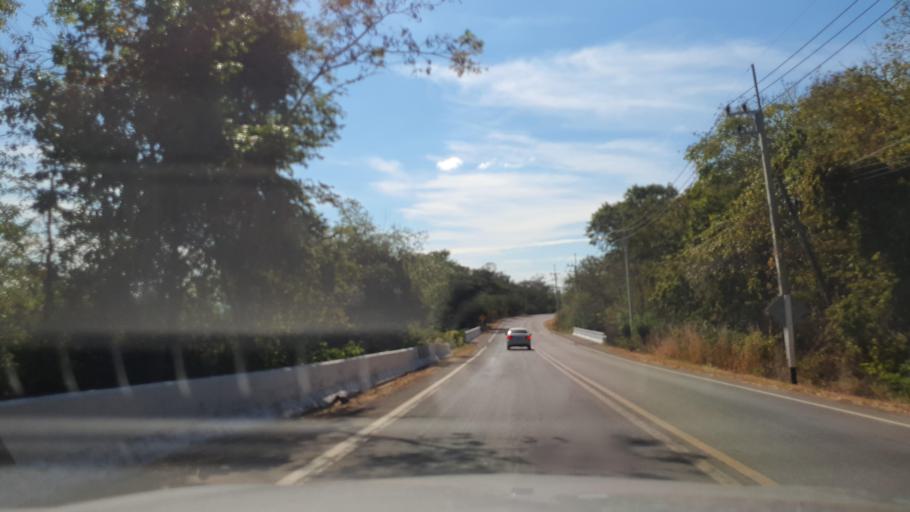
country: TH
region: Kalasin
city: Khao Wong
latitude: 16.7566
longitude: 104.1270
